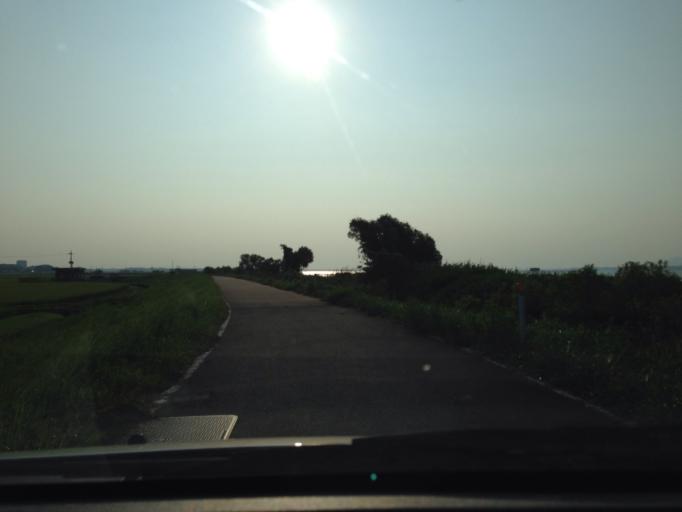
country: JP
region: Ibaraki
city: Inashiki
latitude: 36.0288
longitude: 140.3404
